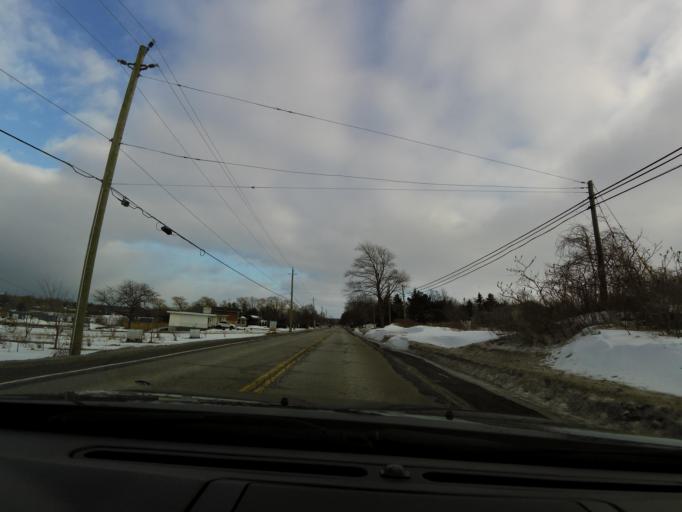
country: CA
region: Ontario
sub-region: Regional Municipality of Niagara
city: St. Catharines
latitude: 43.1742
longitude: -79.5018
